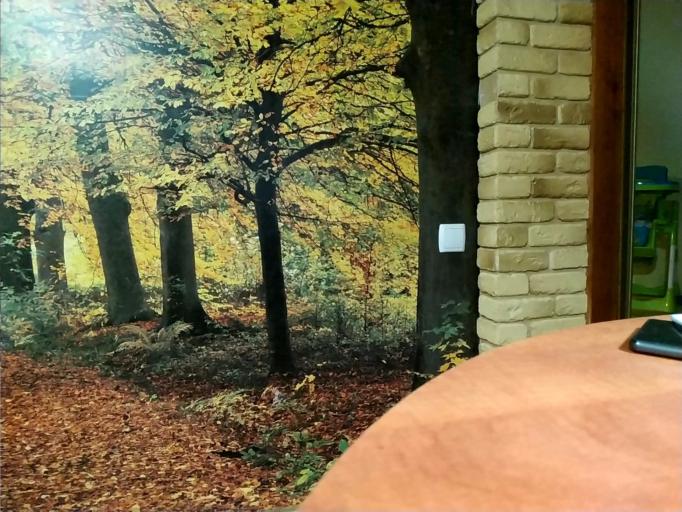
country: BY
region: Minsk
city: Plyeshchanitsy
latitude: 54.4286
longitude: 27.6399
